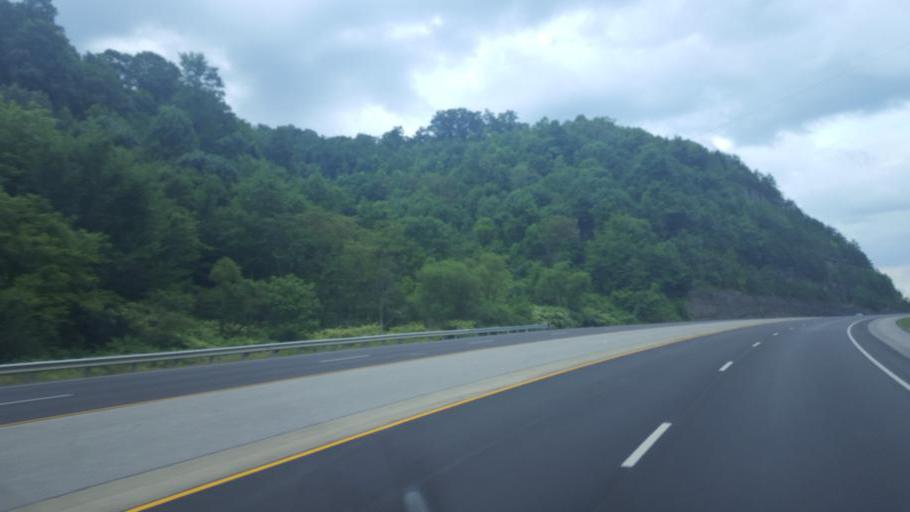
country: US
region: Kentucky
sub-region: Letcher County
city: Jenkins
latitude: 37.2926
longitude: -82.5482
